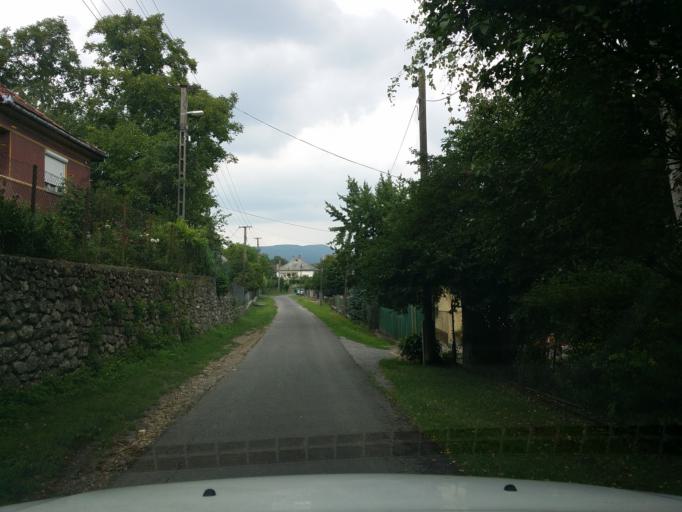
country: HU
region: Borsod-Abauj-Zemplen
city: Sarospatak
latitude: 48.4521
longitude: 21.5267
